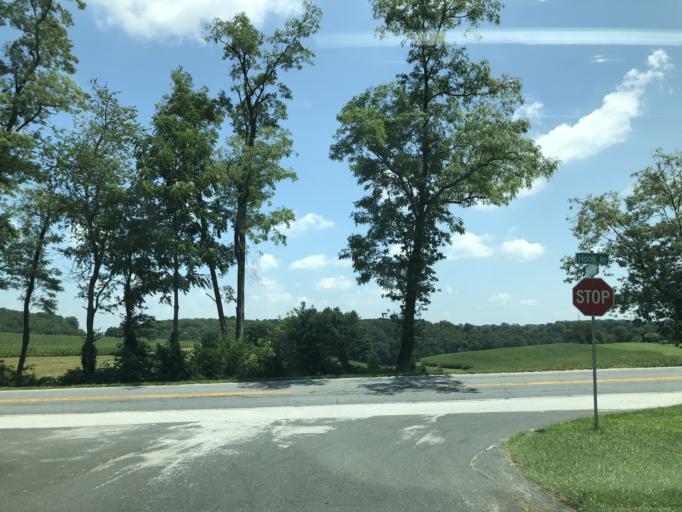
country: US
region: Maryland
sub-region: Carroll County
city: Westminster
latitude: 39.5242
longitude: -76.9513
